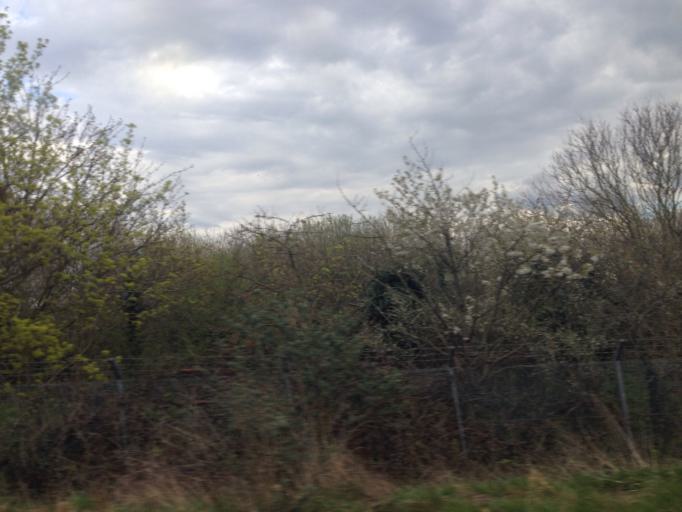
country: GB
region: England
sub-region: Greater London
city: Carshalton
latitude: 51.3817
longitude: -0.1532
